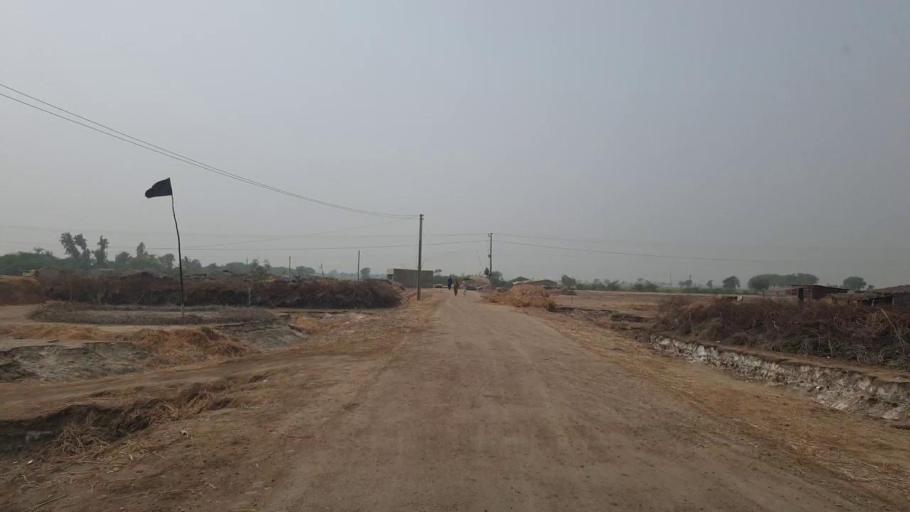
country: PK
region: Sindh
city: Kario
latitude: 24.6562
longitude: 68.6202
